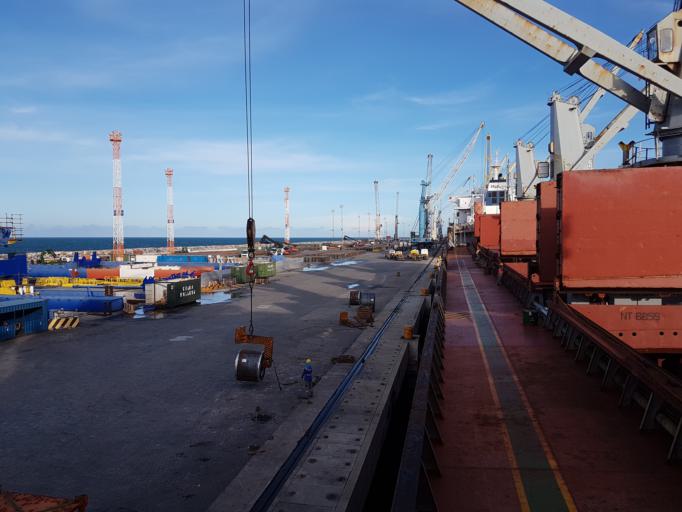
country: BR
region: Ceara
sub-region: Caucaia
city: Cambebba
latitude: -3.5242
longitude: -38.7996
